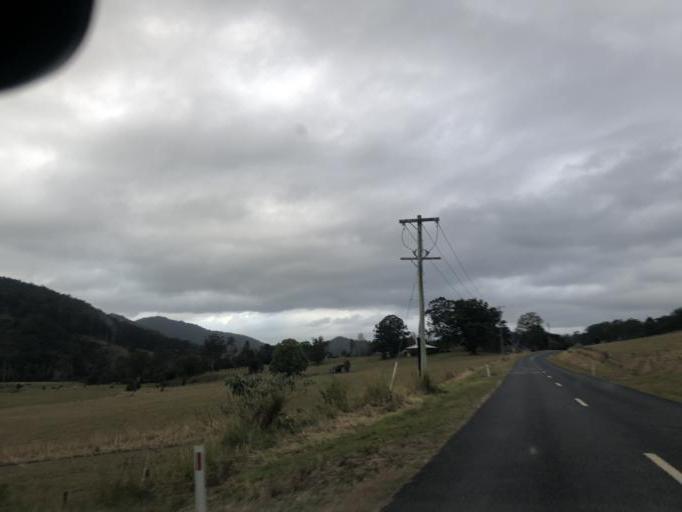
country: AU
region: New South Wales
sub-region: Coffs Harbour
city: Boambee
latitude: -30.2600
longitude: 153.0225
